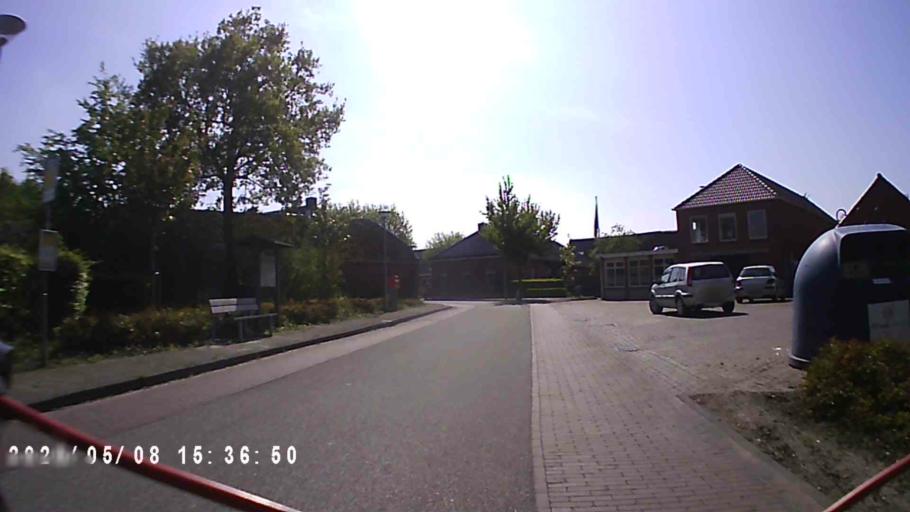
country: NL
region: Groningen
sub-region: Gemeente Bedum
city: Bedum
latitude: 53.3688
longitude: 6.7134
